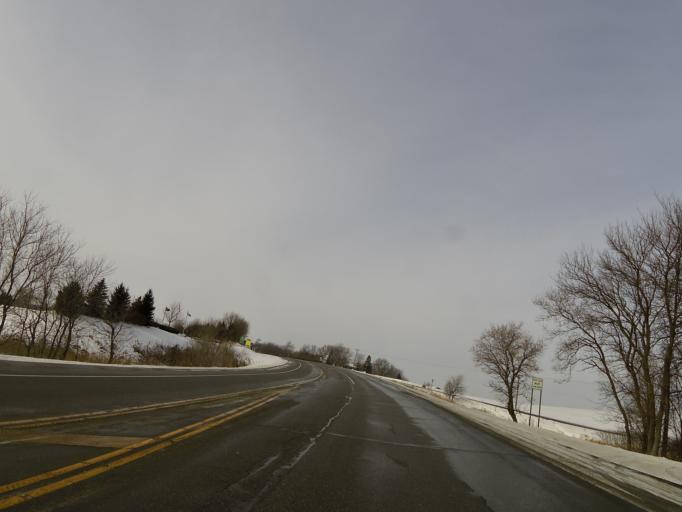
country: US
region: Minnesota
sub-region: Hennepin County
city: Saint Bonifacius
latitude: 44.9048
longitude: -93.7577
